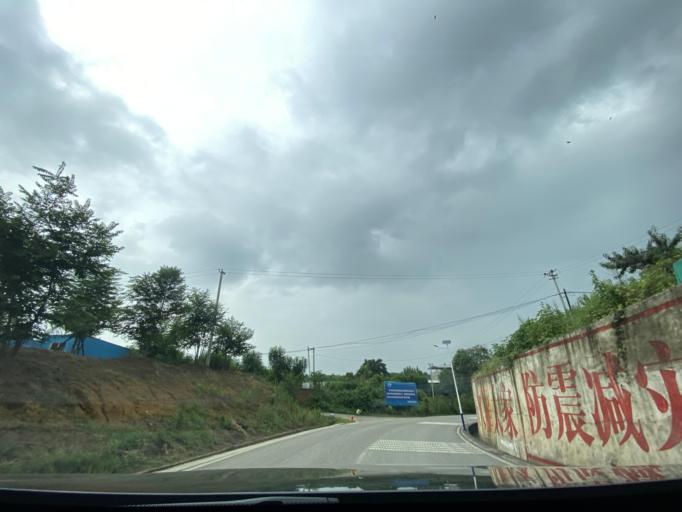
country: CN
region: Sichuan
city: Jiancheng
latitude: 30.5420
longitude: 104.5194
